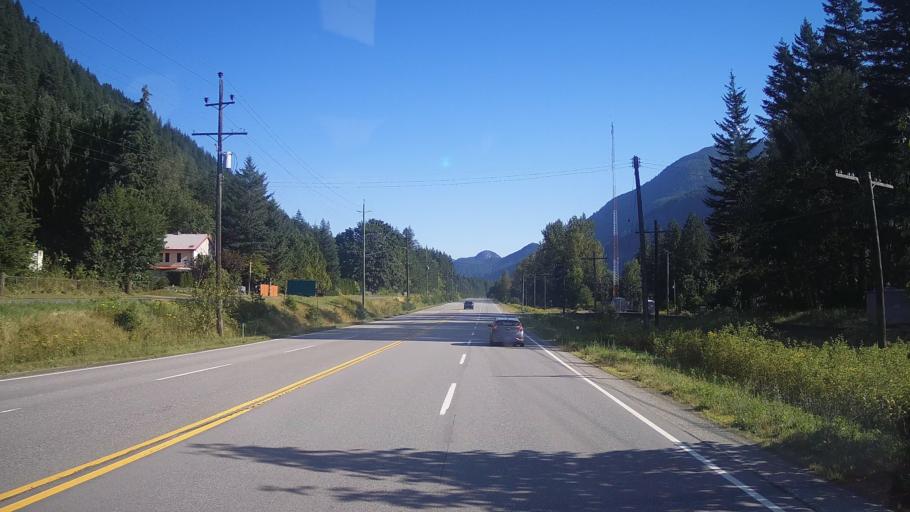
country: CA
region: British Columbia
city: Hope
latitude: 49.4904
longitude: -121.4209
